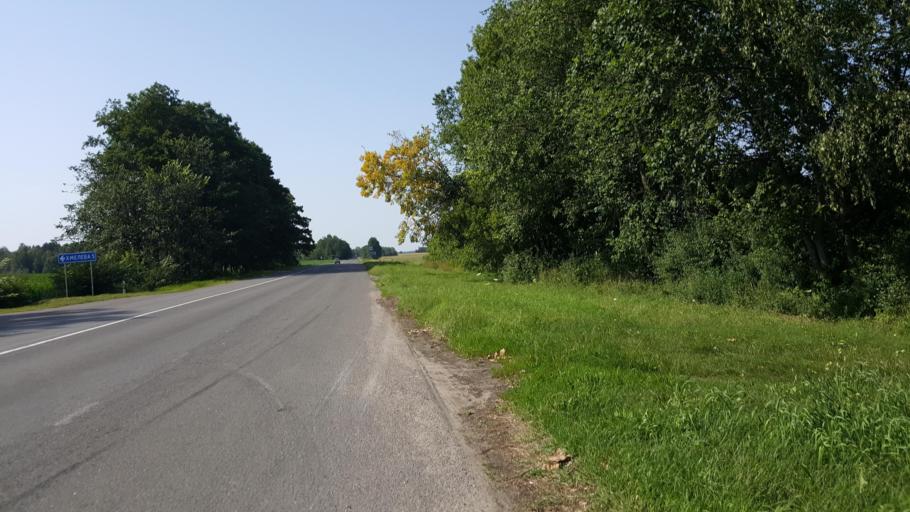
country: BY
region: Brest
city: Zhabinka
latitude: 52.2293
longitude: 23.9860
